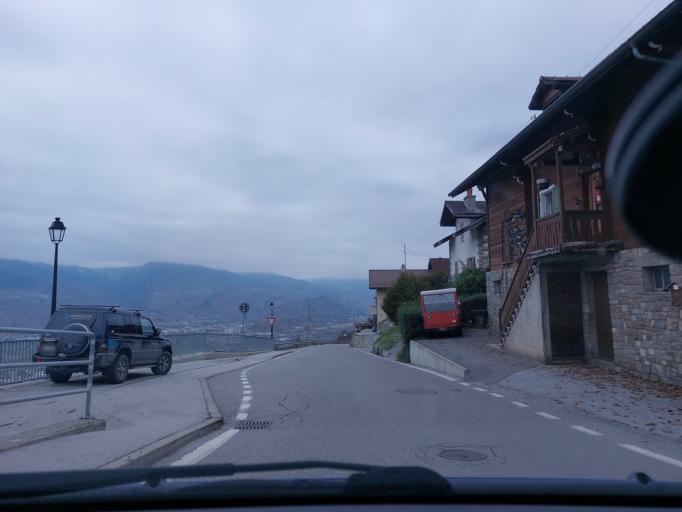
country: CH
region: Valais
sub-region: Conthey District
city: Ardon
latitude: 46.1874
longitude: 7.2706
